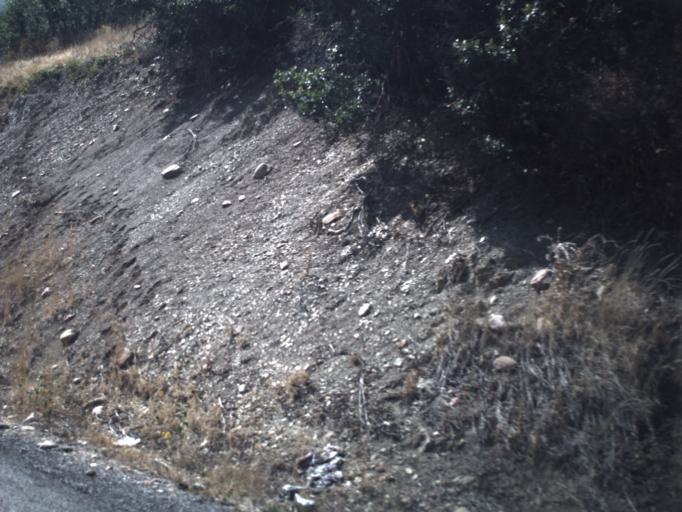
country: US
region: Utah
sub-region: Salt Lake County
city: Mount Olympus
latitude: 40.7466
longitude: -111.7268
